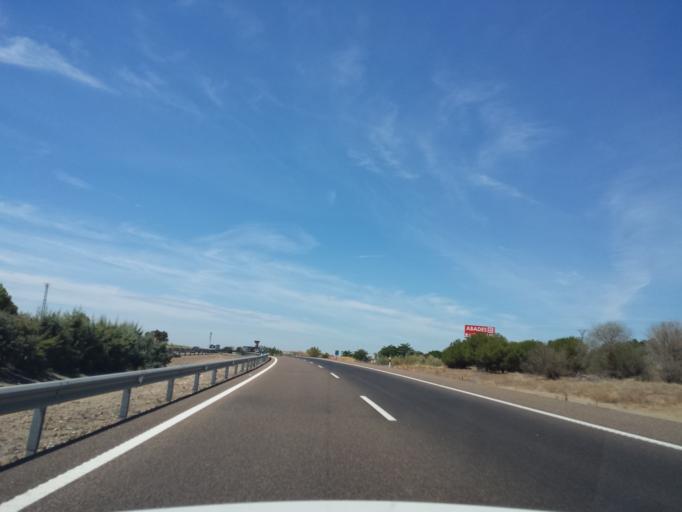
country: ES
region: Extremadura
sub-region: Provincia de Badajoz
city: Trujillanos
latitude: 38.9525
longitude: -6.2476
